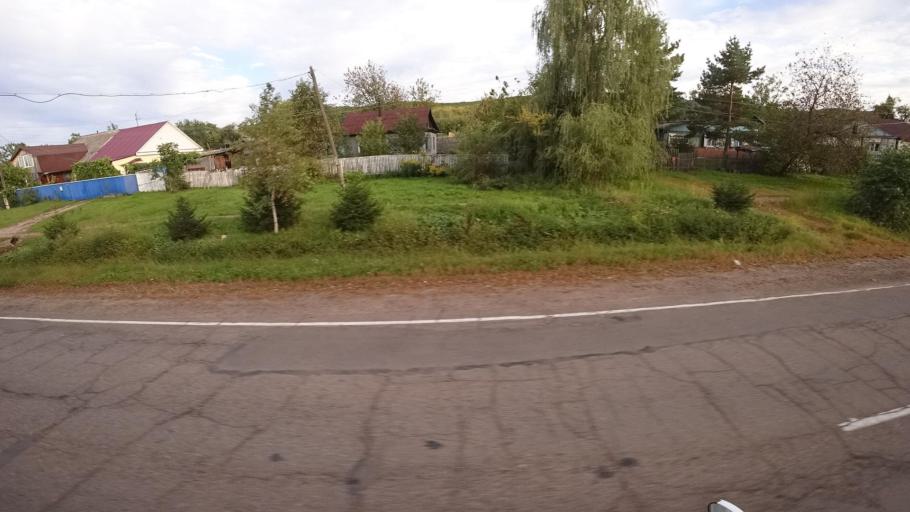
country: RU
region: Primorskiy
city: Yakovlevka
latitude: 44.4208
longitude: 133.4573
